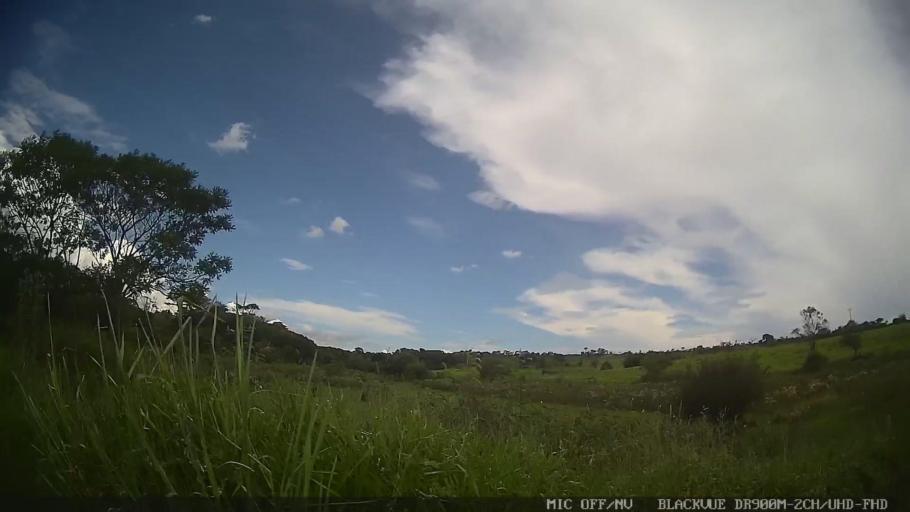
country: BR
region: Sao Paulo
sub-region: Conchas
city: Conchas
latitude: -22.9897
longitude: -47.9960
